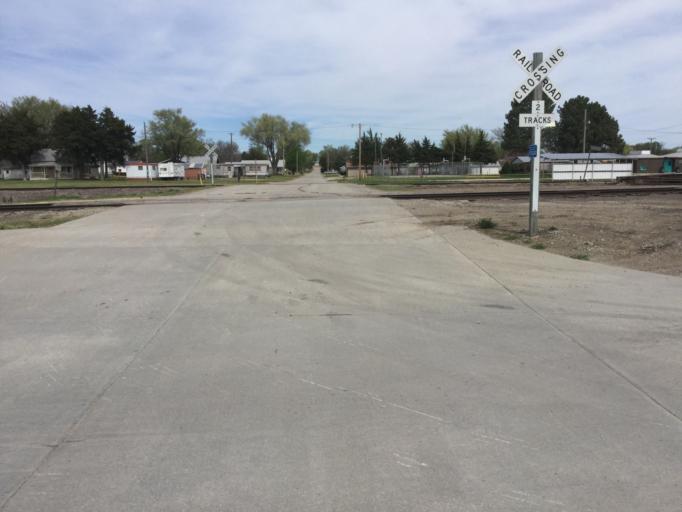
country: US
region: Kansas
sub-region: Osborne County
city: Osborne
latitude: 39.5019
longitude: -98.5462
